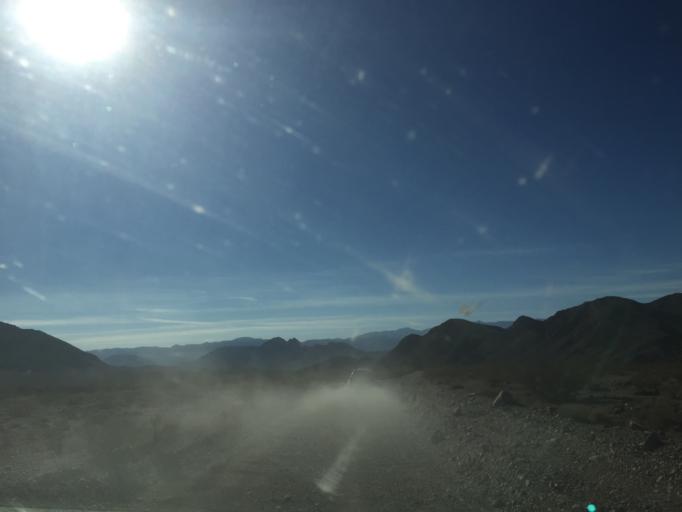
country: US
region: California
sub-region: Inyo County
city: Lone Pine
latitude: 36.7826
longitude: -117.5243
